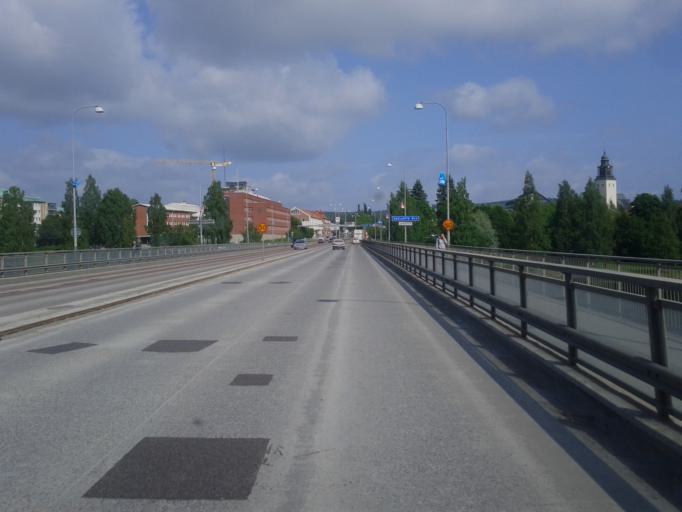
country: SE
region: Vaesterbotten
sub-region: Skelleftea Kommun
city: Skelleftea
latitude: 64.7465
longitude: 20.9599
